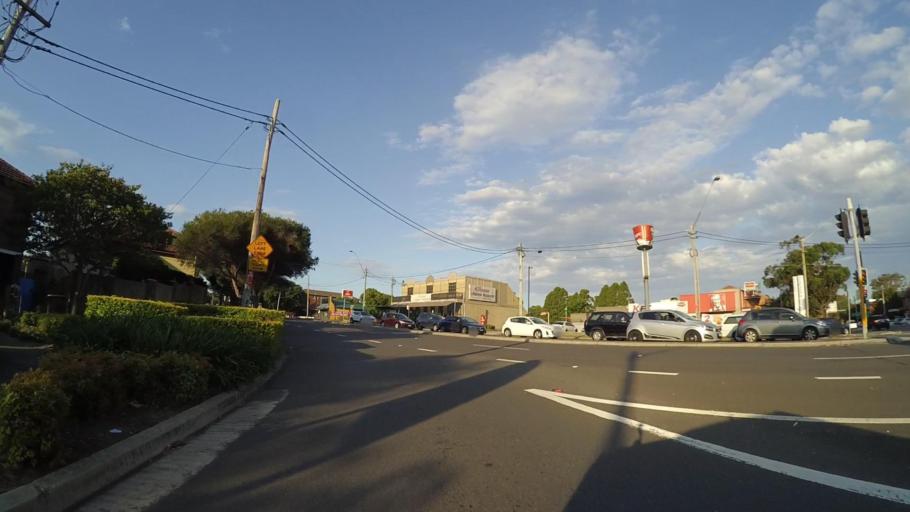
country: AU
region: New South Wales
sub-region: Randwick
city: Daceyville
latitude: -33.9398
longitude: 151.2284
